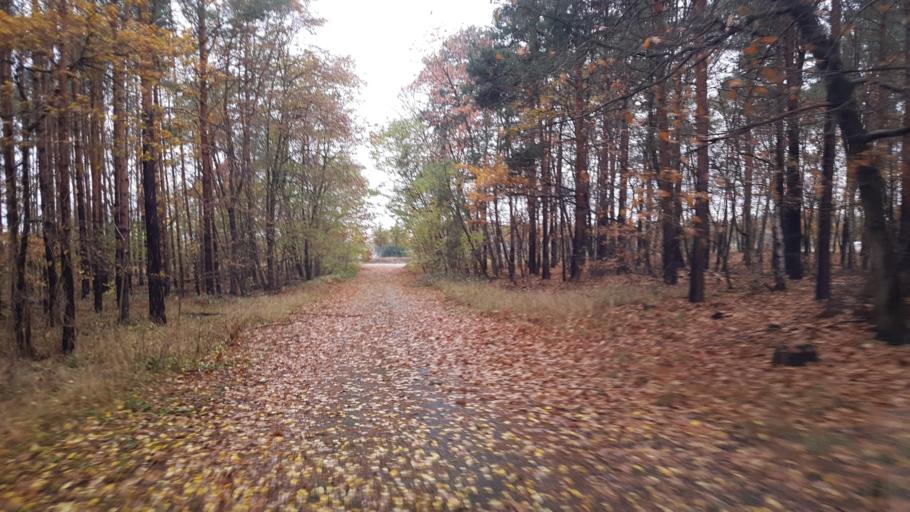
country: DE
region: Brandenburg
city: Drebkau
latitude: 51.6658
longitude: 14.2443
